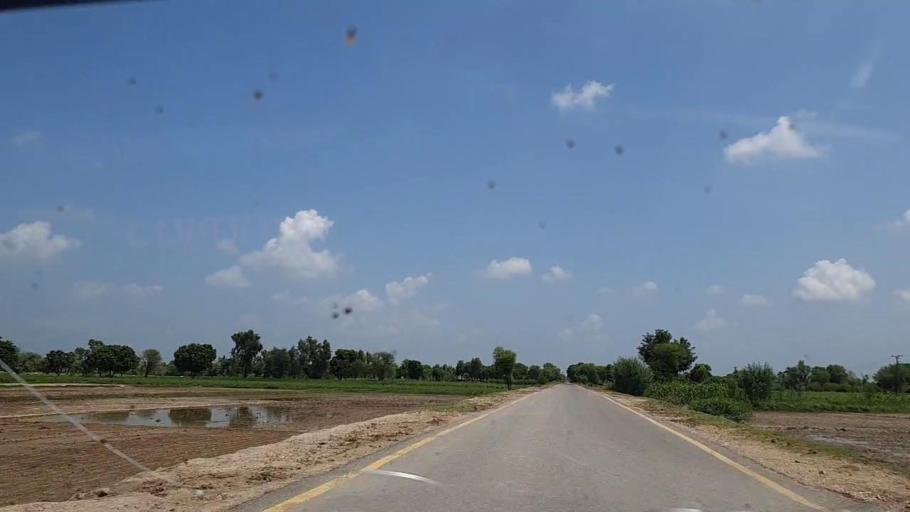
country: PK
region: Sindh
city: Tharu Shah
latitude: 26.9677
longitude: 68.0939
